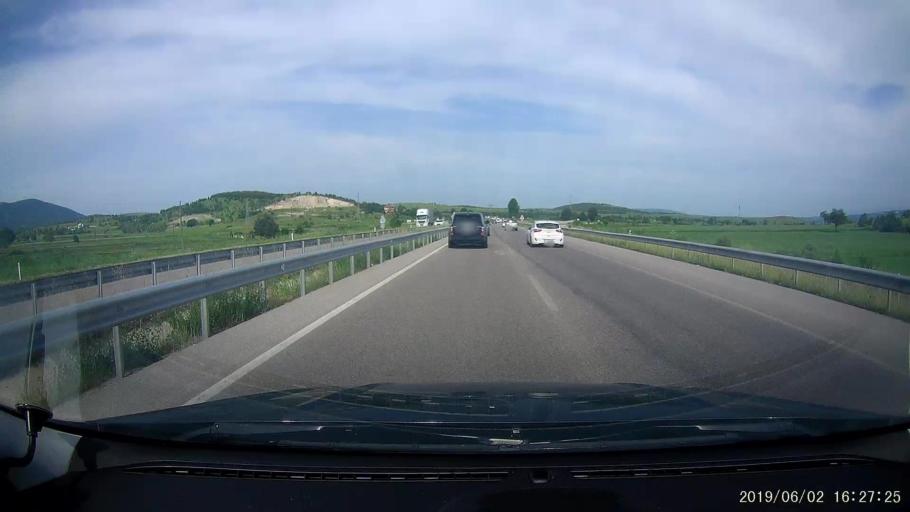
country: TR
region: Samsun
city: Ladik
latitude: 41.0020
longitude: 35.8270
